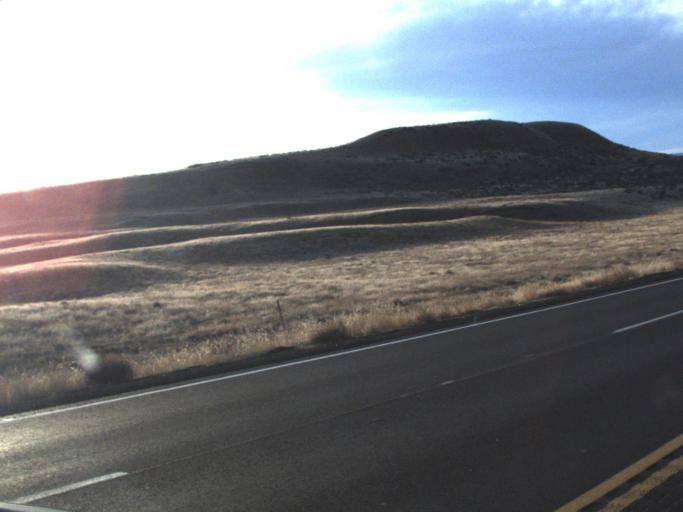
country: US
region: Washington
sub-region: Walla Walla County
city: Burbank
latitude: 46.0683
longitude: -118.7636
